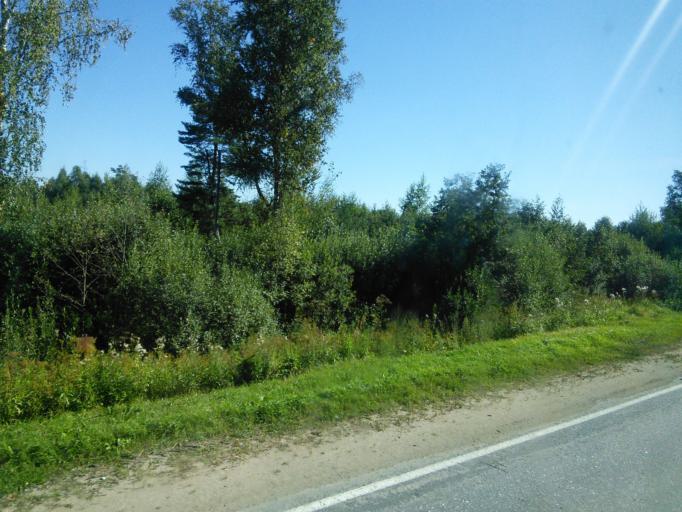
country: RU
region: Jaroslavl
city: Uglich
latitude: 57.4873
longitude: 38.3567
